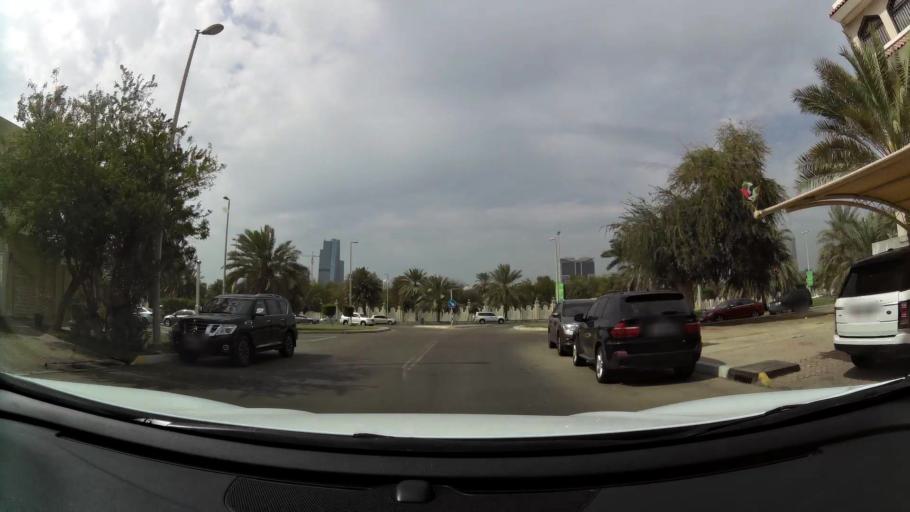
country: AE
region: Abu Dhabi
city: Abu Dhabi
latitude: 24.4688
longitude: 54.3575
